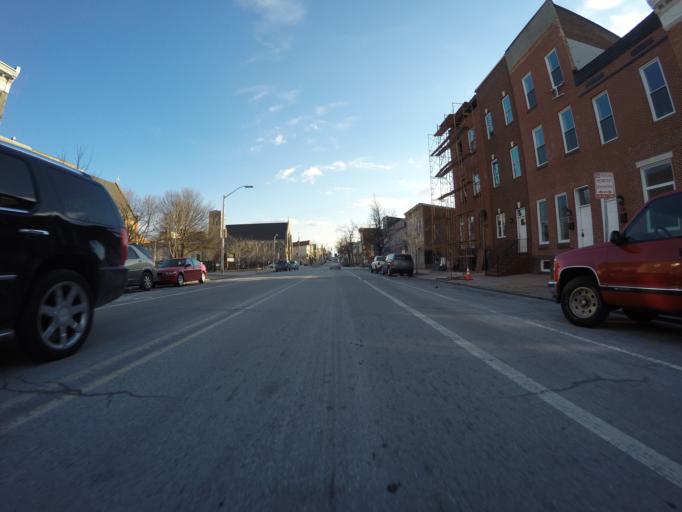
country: US
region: Maryland
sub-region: City of Baltimore
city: Baltimore
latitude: 39.2885
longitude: -76.5691
